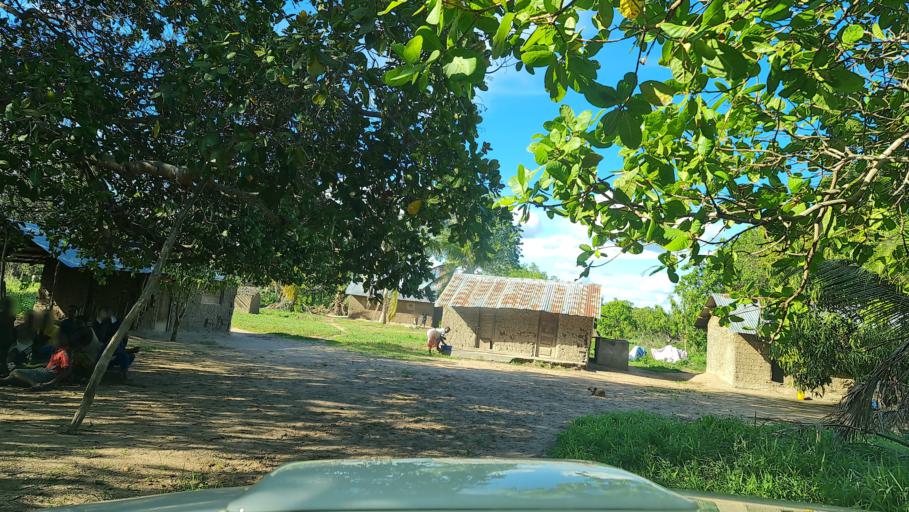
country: MZ
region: Nampula
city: Ilha de Mocambique
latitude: -15.2452
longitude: 40.1797
